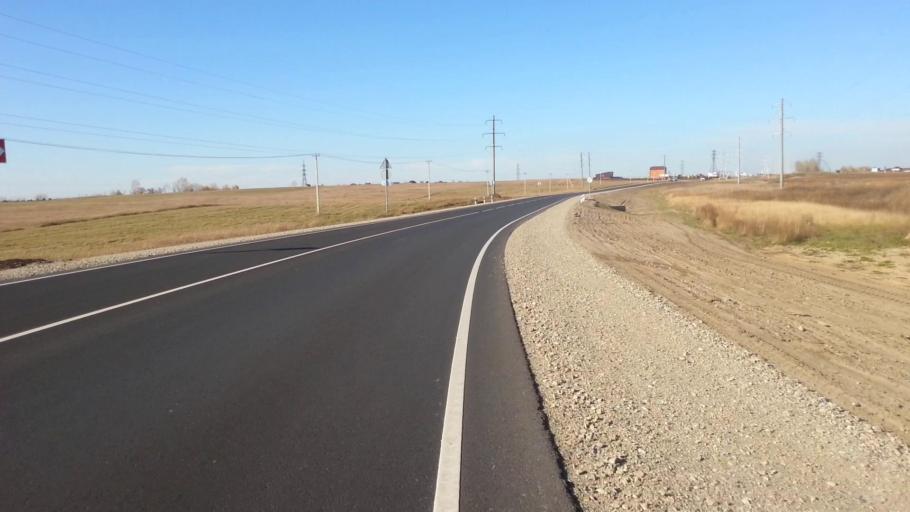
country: RU
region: Altai Krai
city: Sannikovo
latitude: 53.3295
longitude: 83.9389
